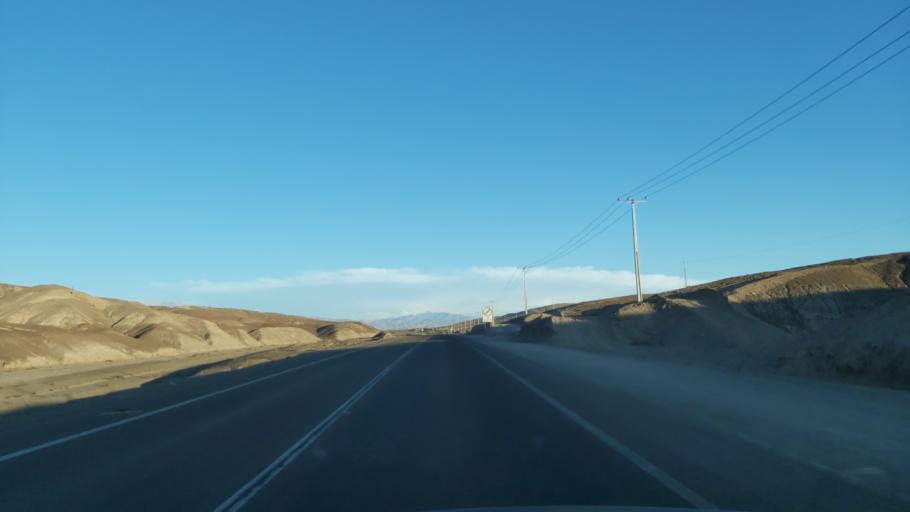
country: CL
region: Atacama
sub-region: Provincia de Chanaral
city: Diego de Almagro
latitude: -26.4200
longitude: -70.0252
